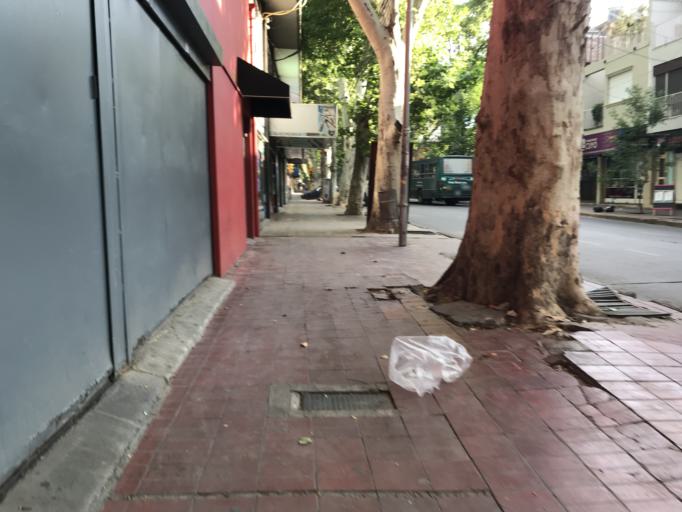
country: AR
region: Mendoza
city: Mendoza
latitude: -32.8881
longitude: -68.8355
